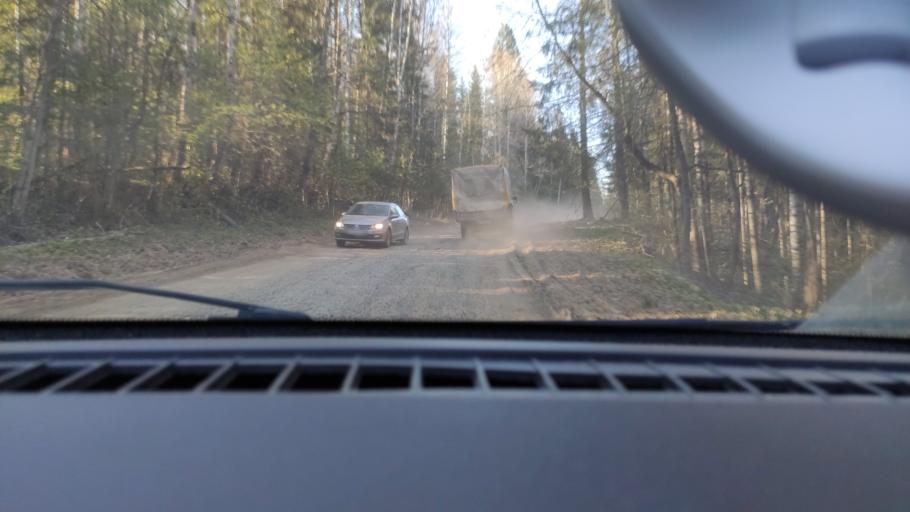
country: RU
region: Perm
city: Novyye Lyady
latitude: 58.1232
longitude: 56.4575
